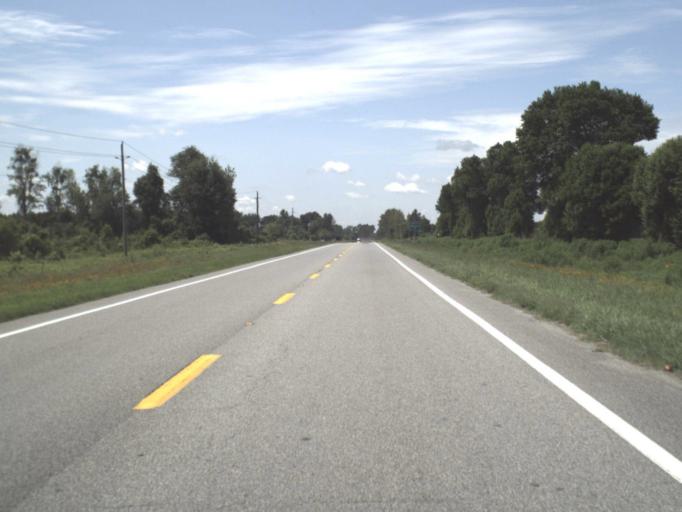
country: US
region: Florida
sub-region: Hamilton County
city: Jasper
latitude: 30.4206
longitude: -82.9337
